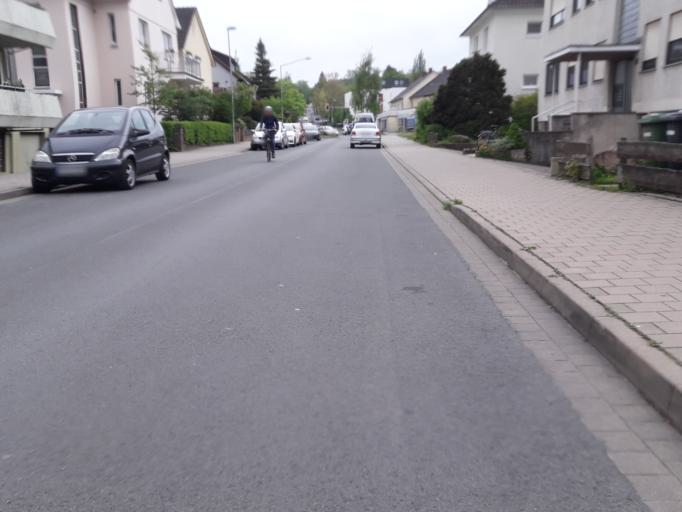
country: DE
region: North Rhine-Westphalia
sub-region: Regierungsbezirk Detmold
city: Detmold
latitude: 51.9375
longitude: 8.8641
